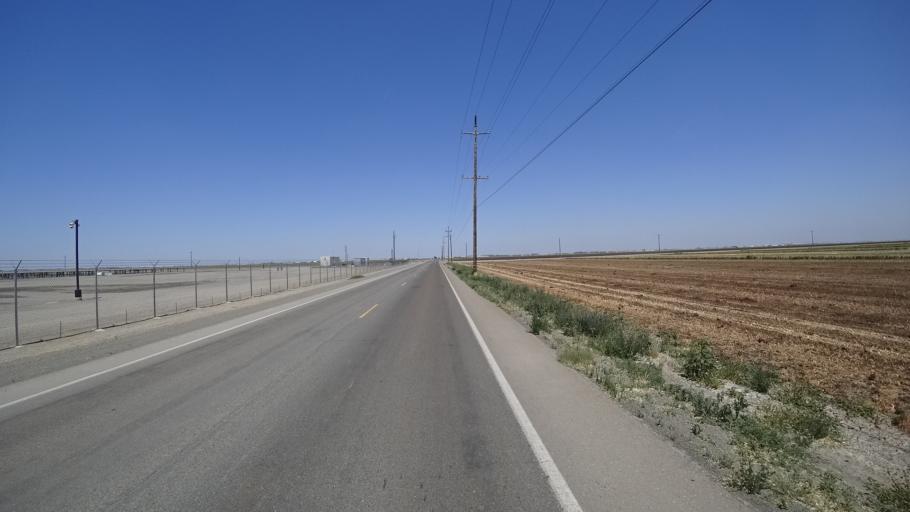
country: US
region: California
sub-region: Kings County
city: Corcoran
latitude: 36.1655
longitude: -119.6459
